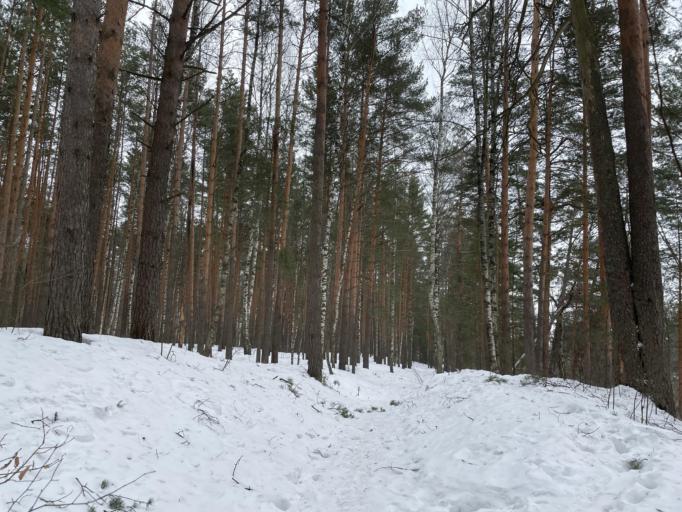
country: RU
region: Vladimir
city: Pokrov
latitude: 55.9393
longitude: 39.2372
